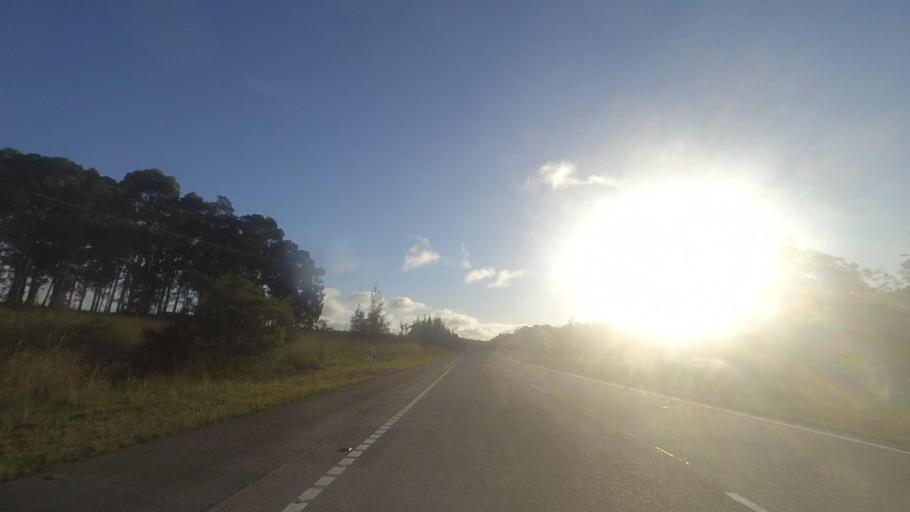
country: AU
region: New South Wales
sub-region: Great Lakes
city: Hawks Nest
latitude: -32.5393
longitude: 152.1691
